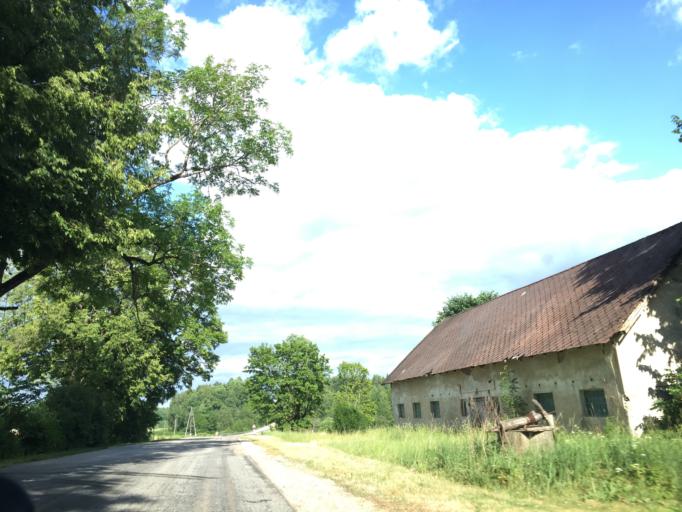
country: LV
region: Skriveri
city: Skriveri
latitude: 56.8035
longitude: 25.0797
